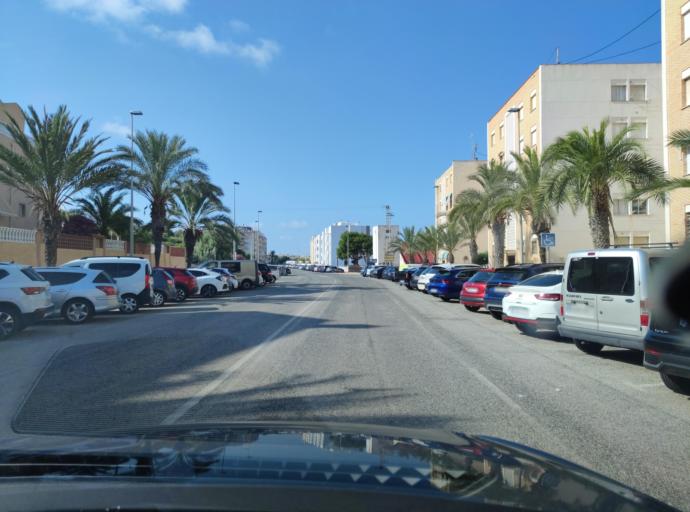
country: ES
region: Valencia
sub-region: Provincia de Alicante
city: Guardamar del Segura
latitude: 38.0771
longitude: -0.6502
